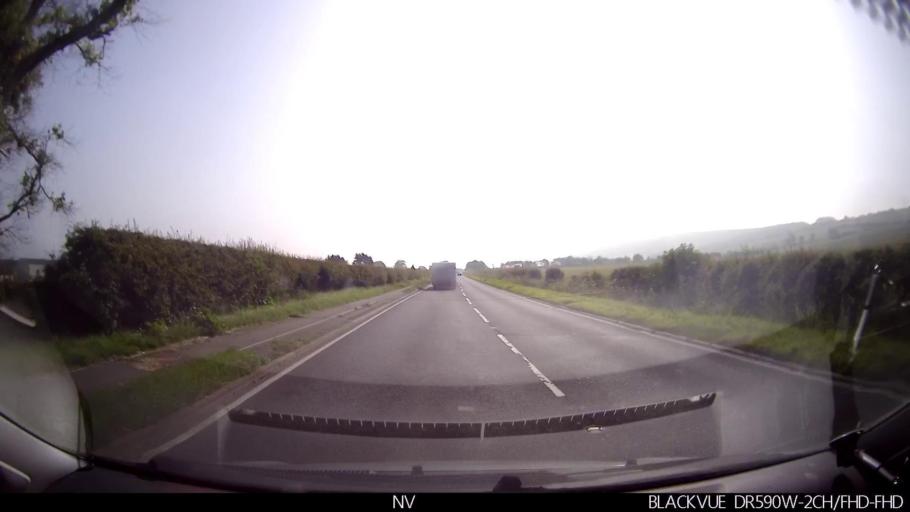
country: GB
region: England
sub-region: North Yorkshire
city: East Ayton
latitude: 54.1943
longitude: -0.4650
